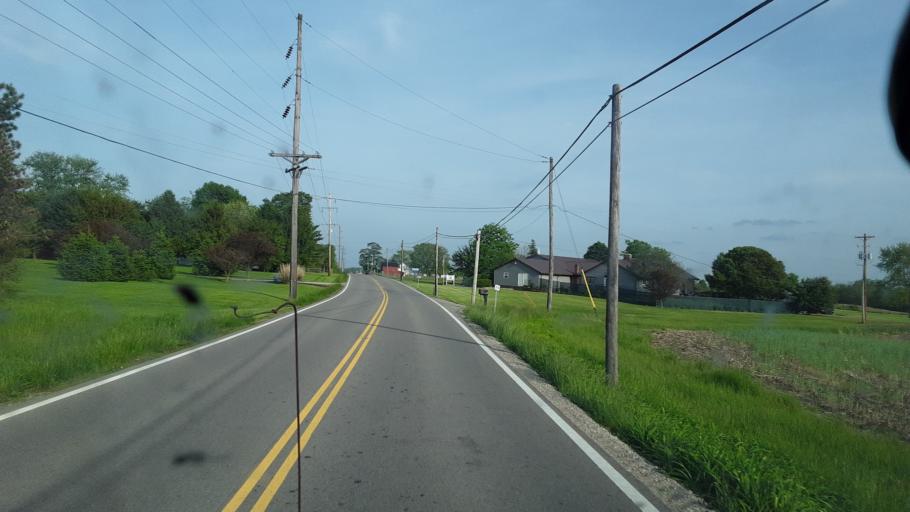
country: US
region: Ohio
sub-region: Pickaway County
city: Logan Elm Village
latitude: 39.5582
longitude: -82.8729
